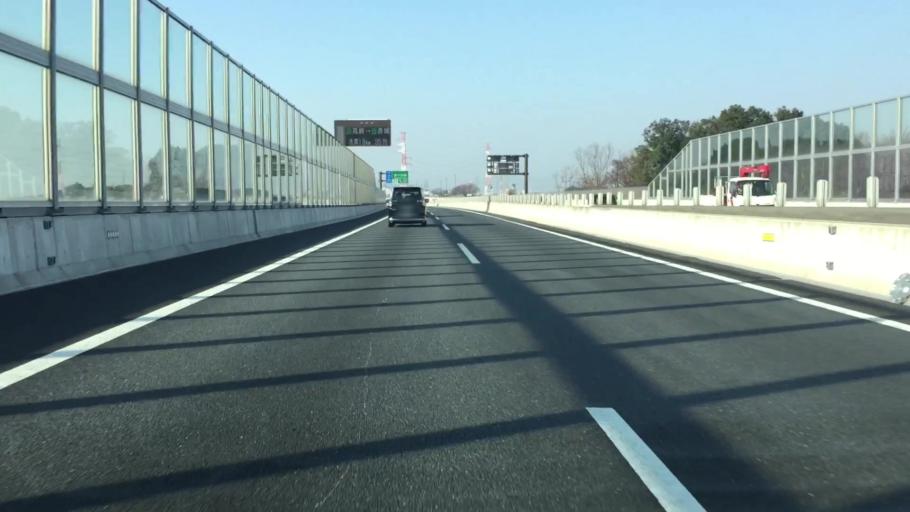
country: JP
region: Saitama
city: Okegawa
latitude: 36.0243
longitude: 139.5708
